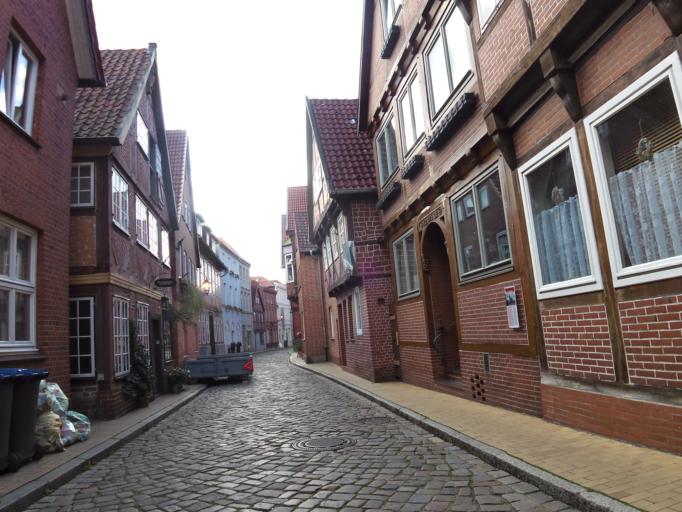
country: DE
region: Schleswig-Holstein
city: Lauenburg
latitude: 53.3704
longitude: 10.5542
